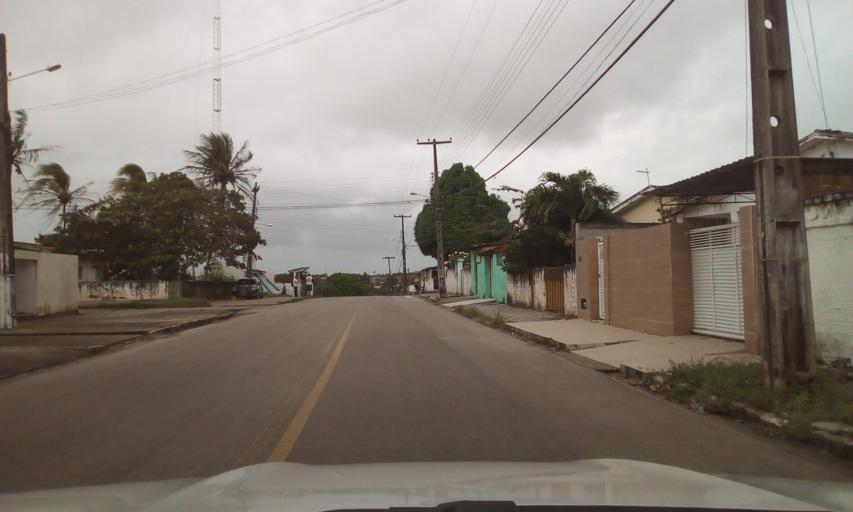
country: BR
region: Paraiba
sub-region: Joao Pessoa
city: Joao Pessoa
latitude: -7.1619
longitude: -34.8905
